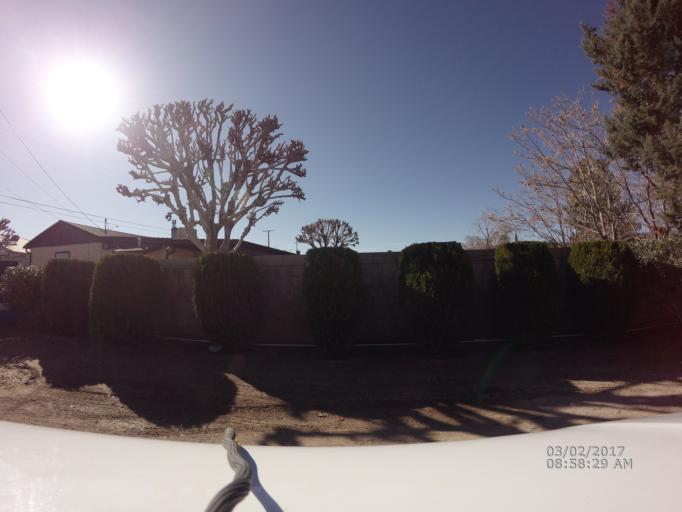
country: US
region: California
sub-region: Los Angeles County
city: Quartz Hill
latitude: 34.6418
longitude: -118.2103
